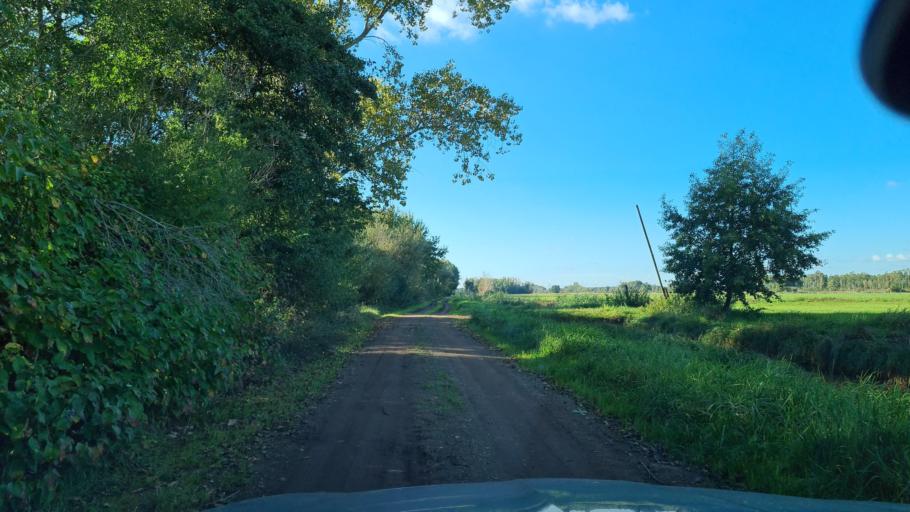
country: DE
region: Brandenburg
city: Bad Liebenwerda
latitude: 51.5227
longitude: 13.3667
